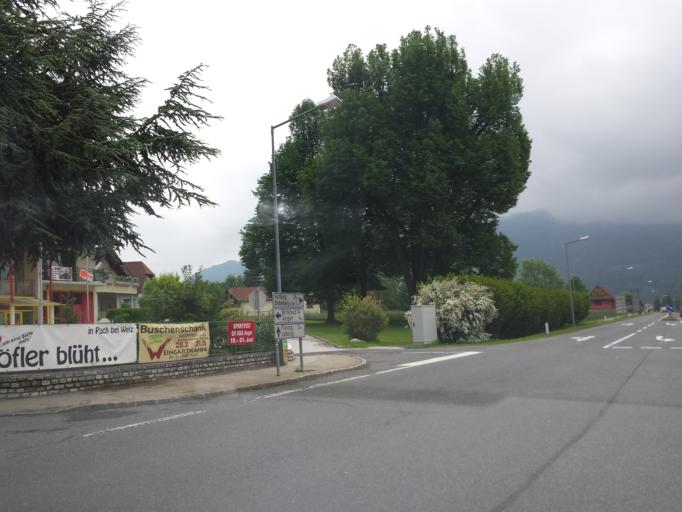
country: AT
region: Styria
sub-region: Politischer Bezirk Weiz
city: Floing
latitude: 47.2485
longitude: 15.7296
